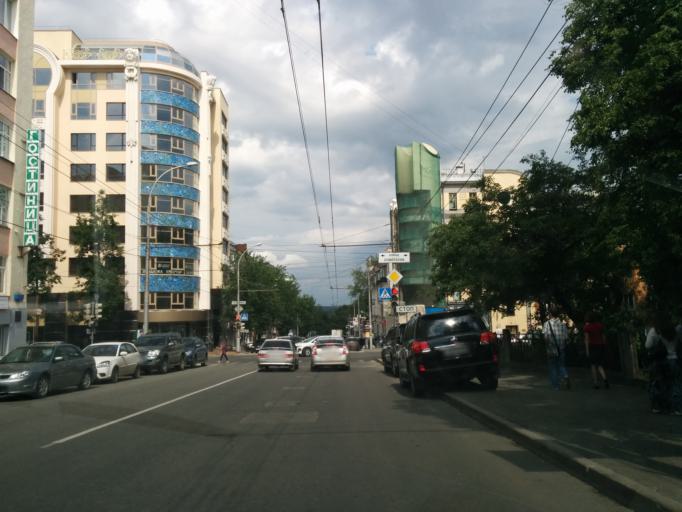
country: RU
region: Perm
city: Perm
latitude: 58.0159
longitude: 56.2442
